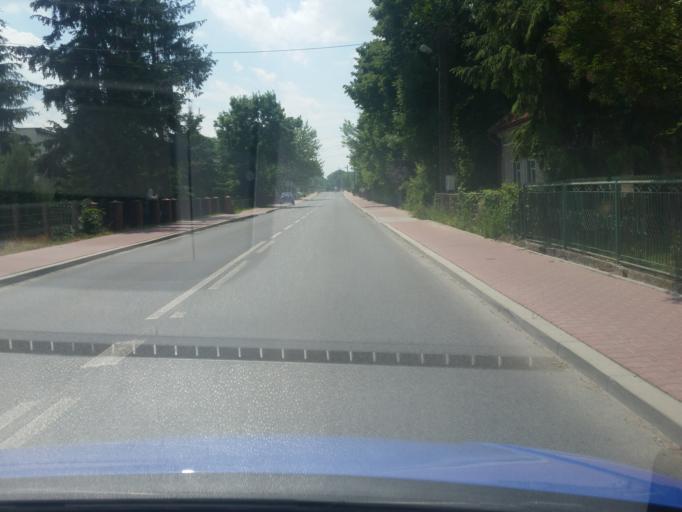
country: PL
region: Swietokrzyskie
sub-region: Powiat buski
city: Wislica
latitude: 50.3444
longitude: 20.6675
